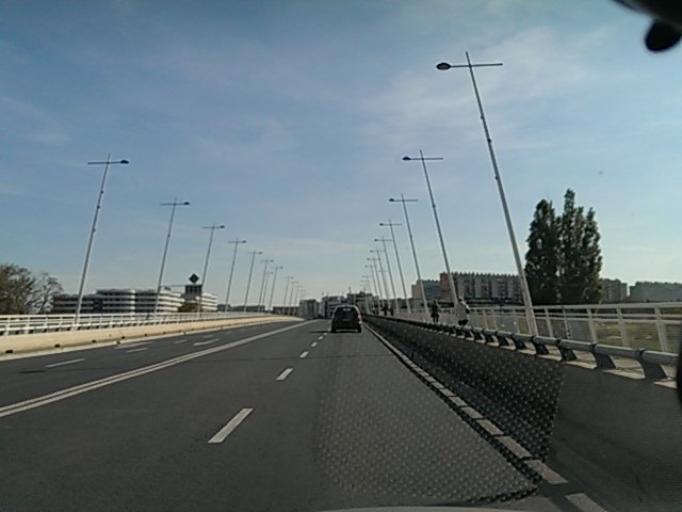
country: PL
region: Subcarpathian Voivodeship
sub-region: Rzeszow
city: Rzeszow
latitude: 50.0310
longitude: 22.0036
